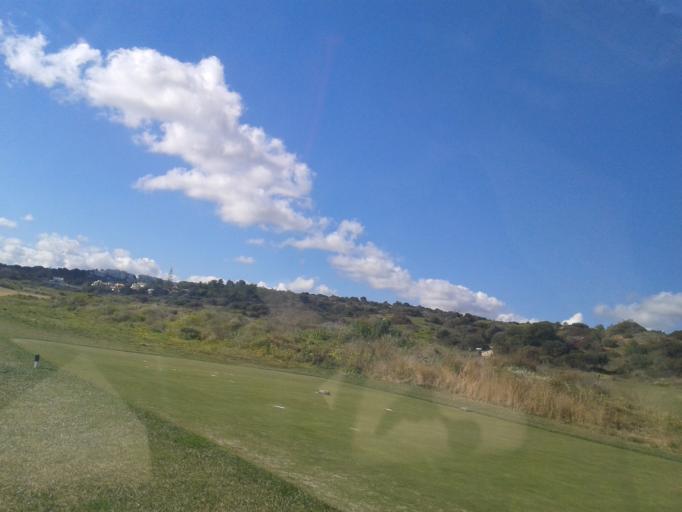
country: PT
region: Faro
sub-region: Lagos
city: Lagos
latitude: 37.1225
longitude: -8.6378
